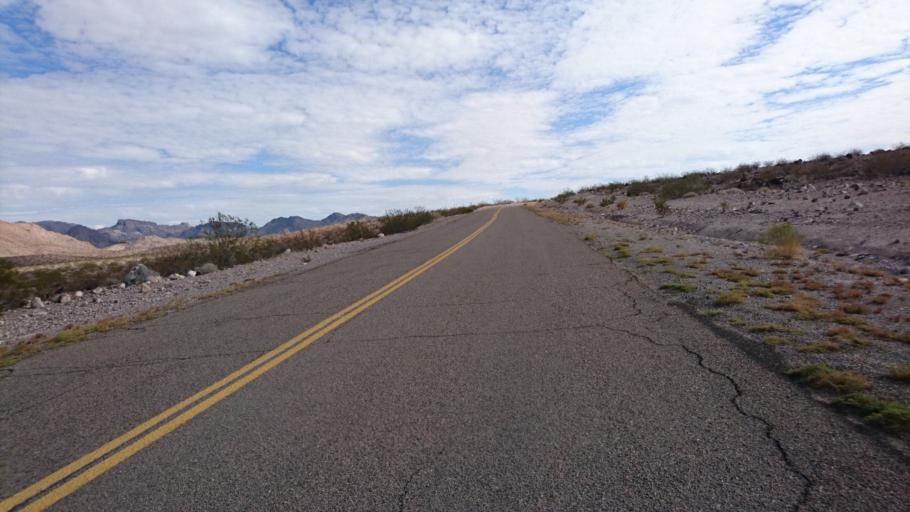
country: US
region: Arizona
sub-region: Mohave County
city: Mohave Valley
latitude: 34.9045
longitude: -114.4296
